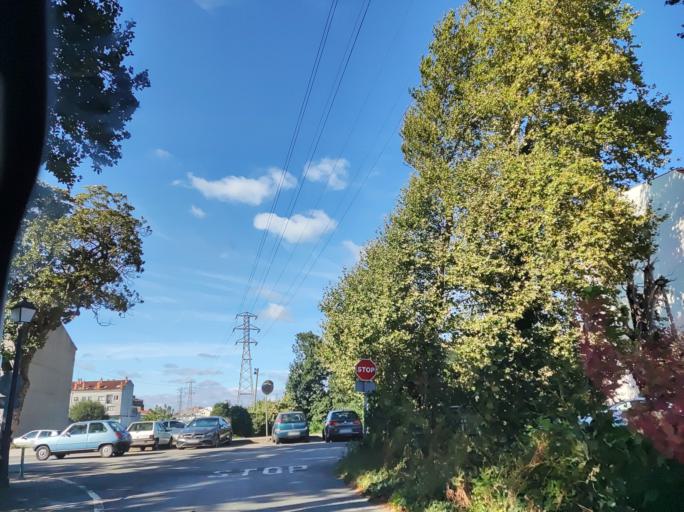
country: ES
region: Galicia
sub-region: Provincia da Coruna
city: Padron
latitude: 42.7387
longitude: -8.6574
